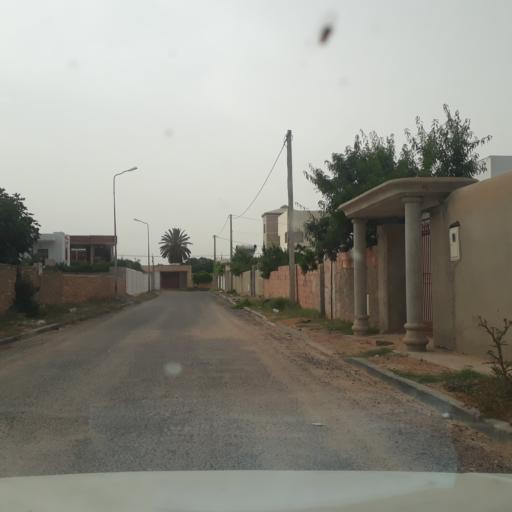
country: TN
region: Safaqis
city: Al Qarmadah
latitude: 34.8135
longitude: 10.7665
